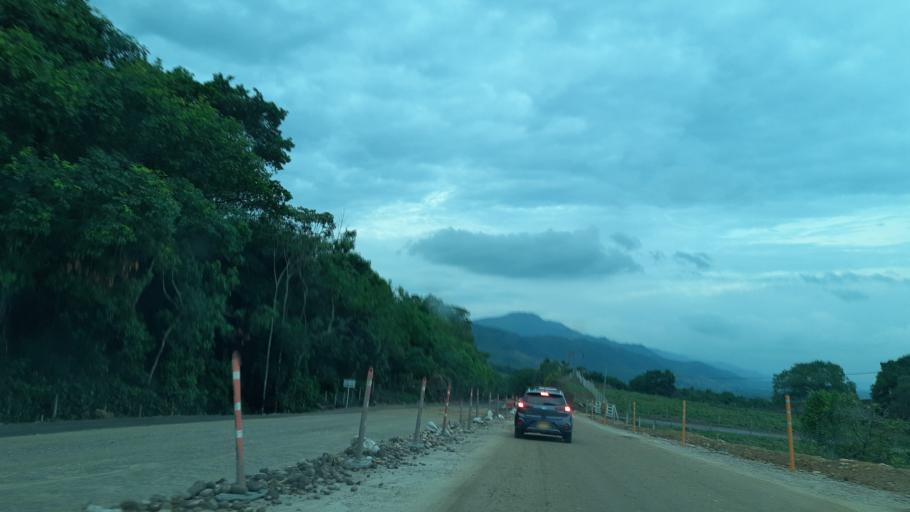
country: CO
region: Casanare
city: Sabanalarga
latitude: 4.7560
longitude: -73.0088
